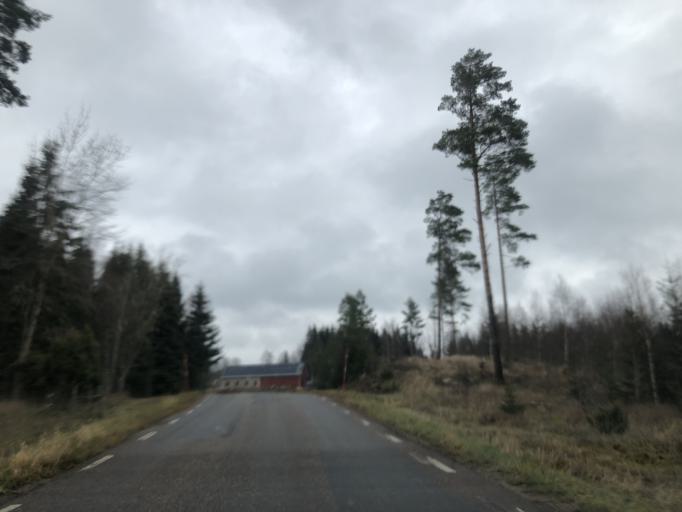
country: SE
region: Vaestra Goetaland
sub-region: Ulricehamns Kommun
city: Ulricehamn
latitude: 57.8704
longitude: 13.5456
